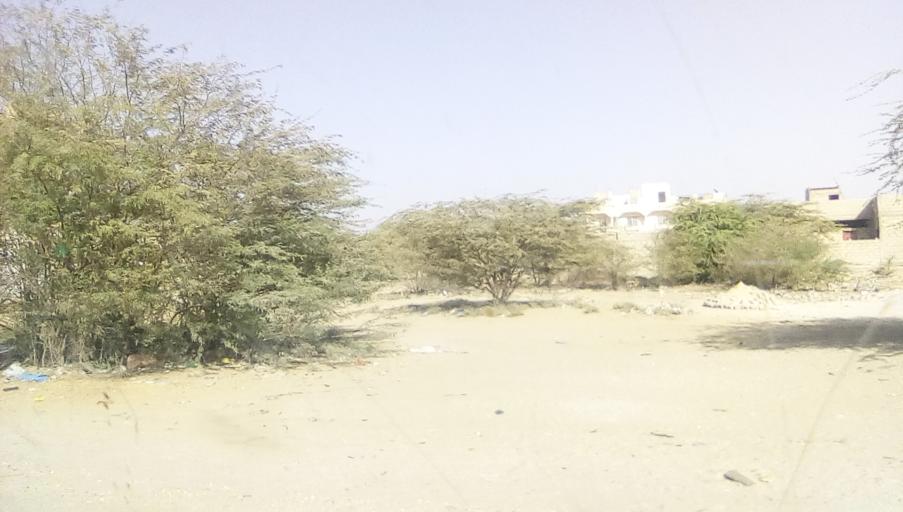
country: SN
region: Saint-Louis
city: Saint-Louis
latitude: 16.0471
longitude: -16.4346
